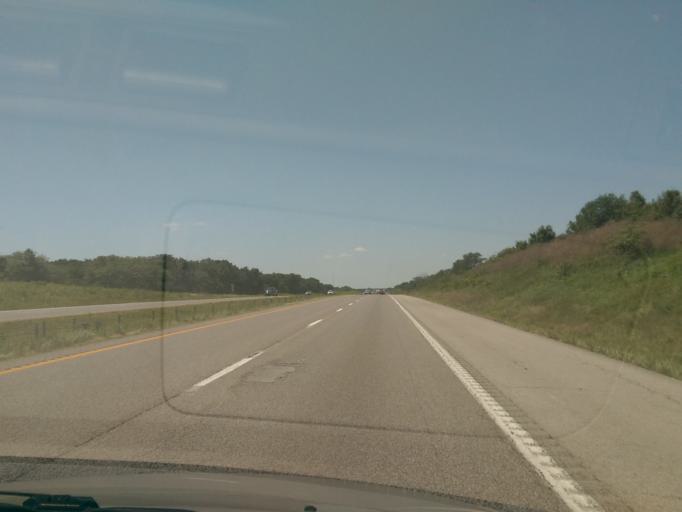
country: US
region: Missouri
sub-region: Saline County
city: Marshall
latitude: 38.9510
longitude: -93.0559
